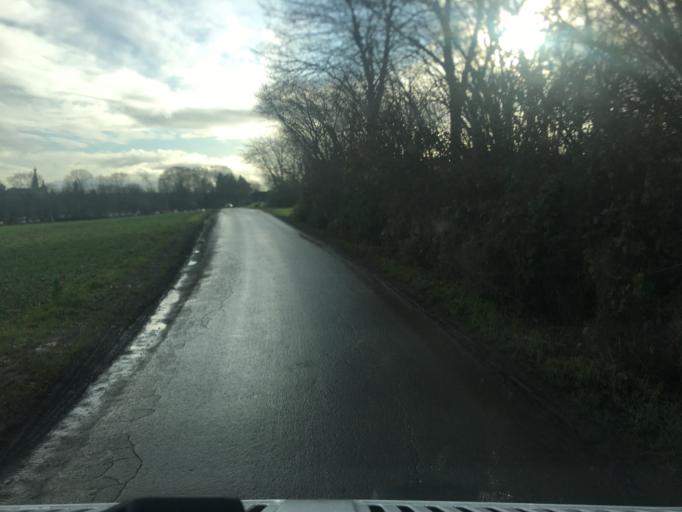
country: DE
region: North Rhine-Westphalia
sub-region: Regierungsbezirk Koln
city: Langerwehe
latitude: 50.8024
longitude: 6.3821
